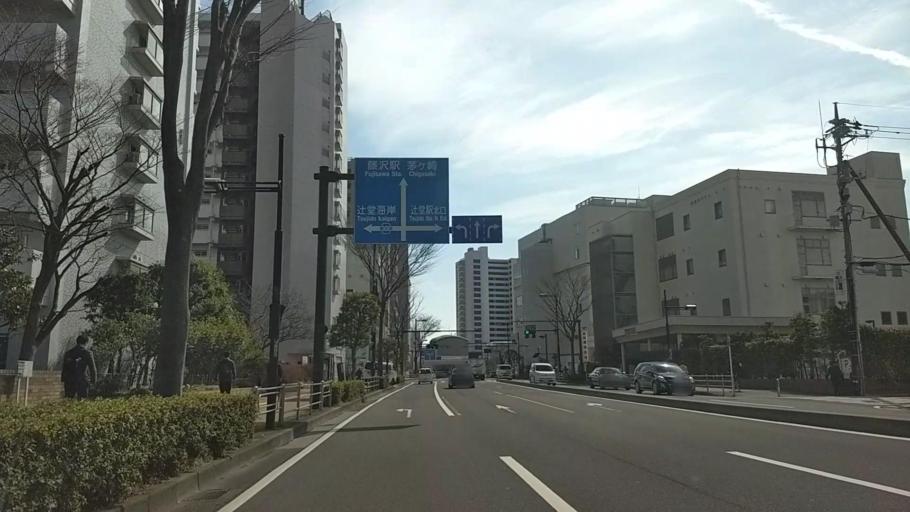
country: JP
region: Kanagawa
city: Fujisawa
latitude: 35.3396
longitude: 139.4489
